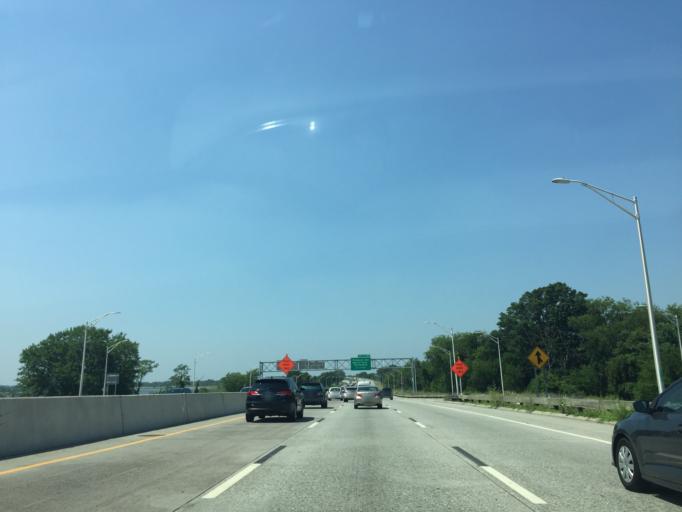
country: US
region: New York
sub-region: Kings County
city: East New York
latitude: 40.6300
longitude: -73.8867
